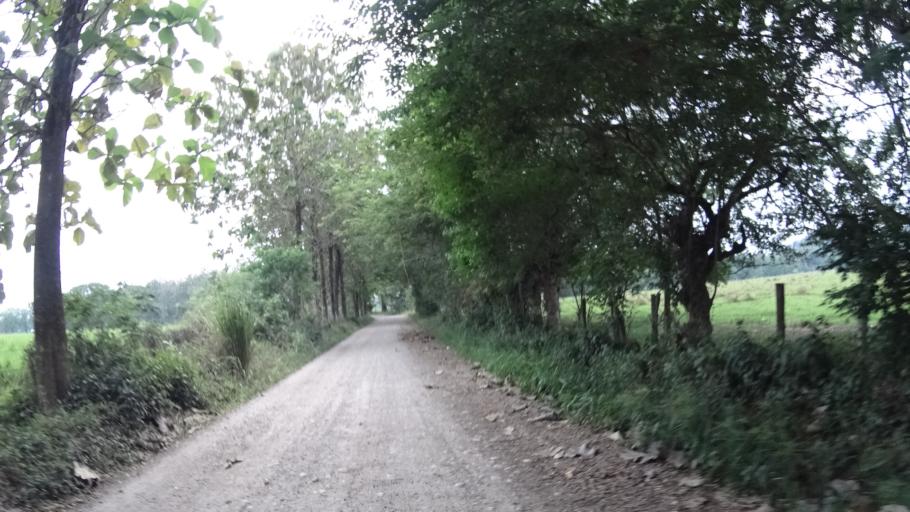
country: CO
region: Cundinamarca
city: Puerto Salgar
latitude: 5.4865
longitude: -74.6956
